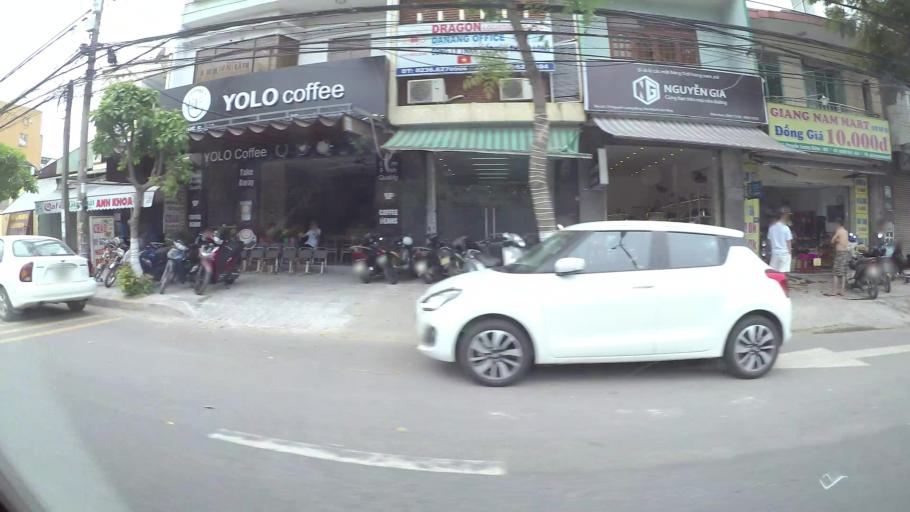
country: VN
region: Da Nang
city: Lien Chieu
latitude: 16.0742
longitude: 108.1493
